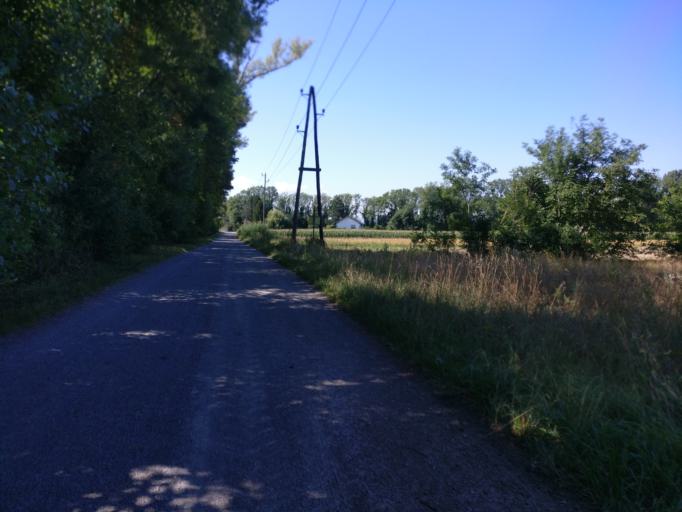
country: AT
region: Lower Austria
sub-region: Politischer Bezirk Baden
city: Pottendorf
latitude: 47.9071
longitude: 16.3523
